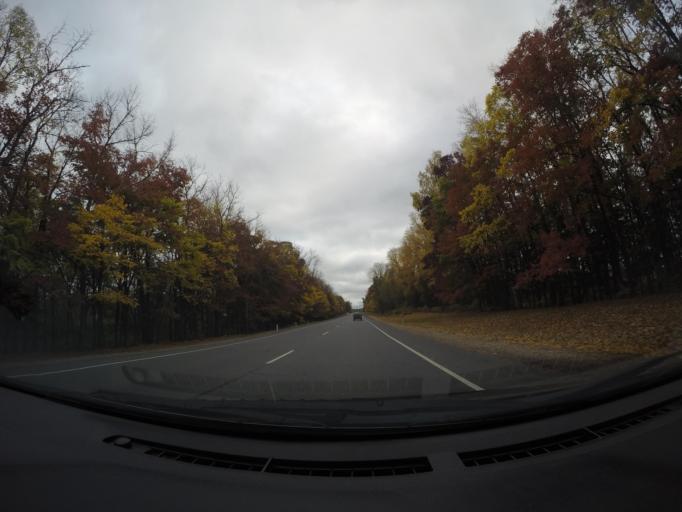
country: RU
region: Moskovskaya
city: Dorokhovo
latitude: 55.5878
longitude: 36.3679
